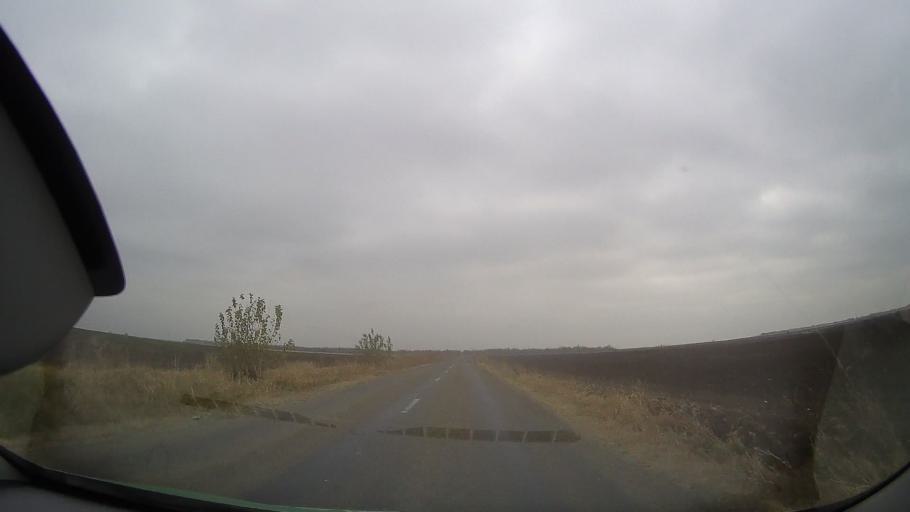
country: RO
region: Buzau
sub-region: Comuna Bradeanu
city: Bradeanu
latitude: 44.8937
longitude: 26.8736
